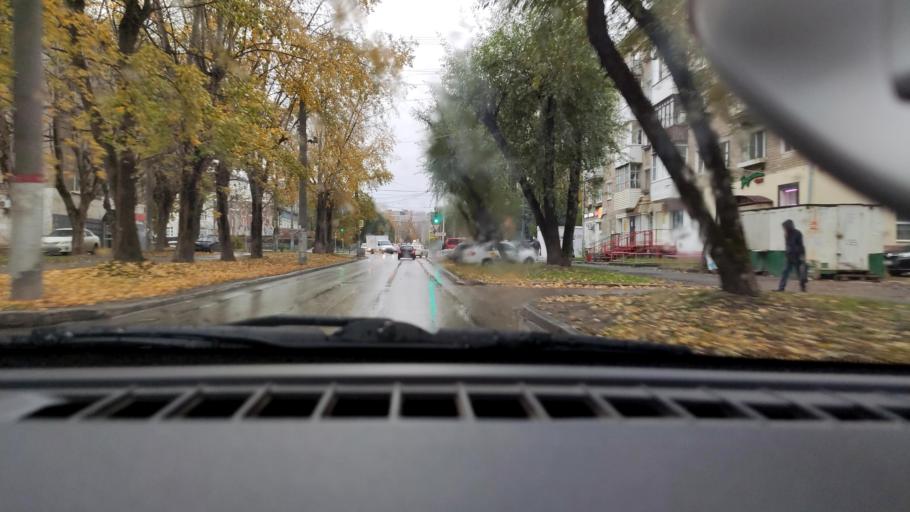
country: RU
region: Perm
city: Perm
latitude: 57.9812
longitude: 56.1926
